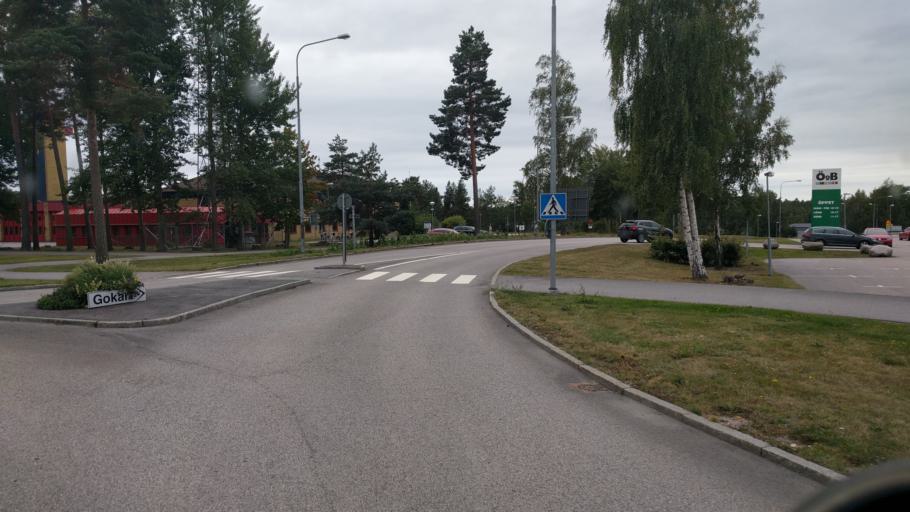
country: SE
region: Kalmar
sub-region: Vasterviks Kommun
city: Vaestervik
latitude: 57.7511
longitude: 16.6312
